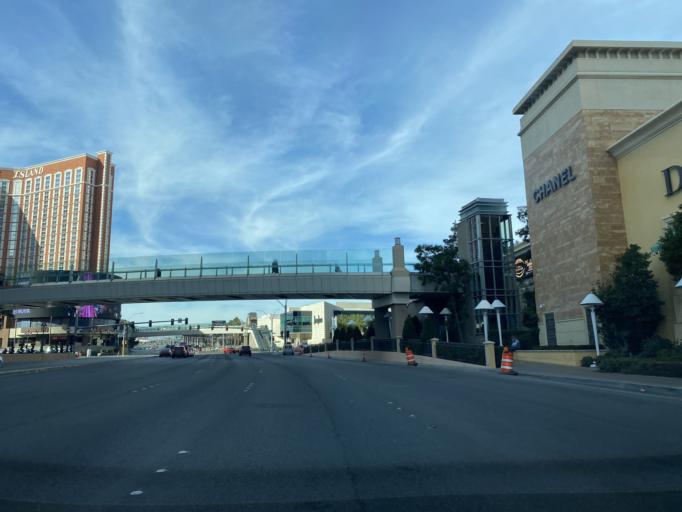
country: US
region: Nevada
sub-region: Clark County
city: Paradise
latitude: 36.1253
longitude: -115.1678
